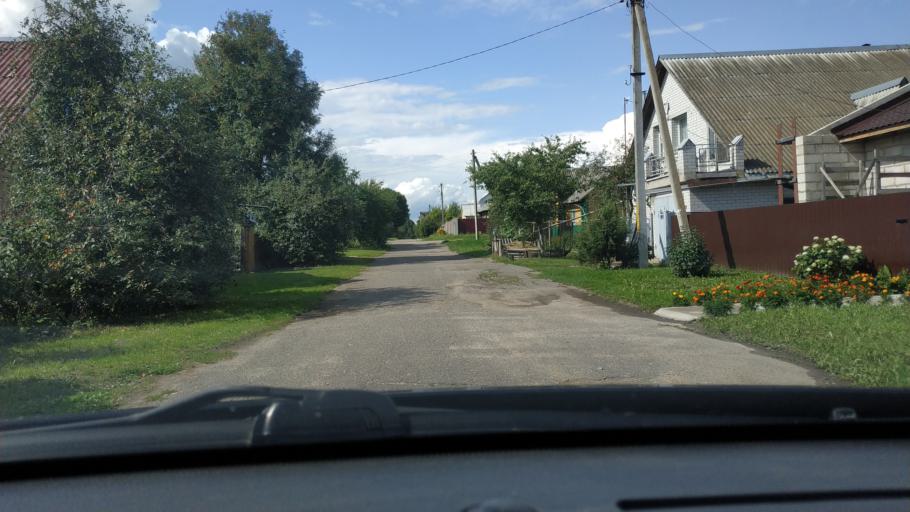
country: BY
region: Mogilev
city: Mahilyow
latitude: 53.9025
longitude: 30.2921
